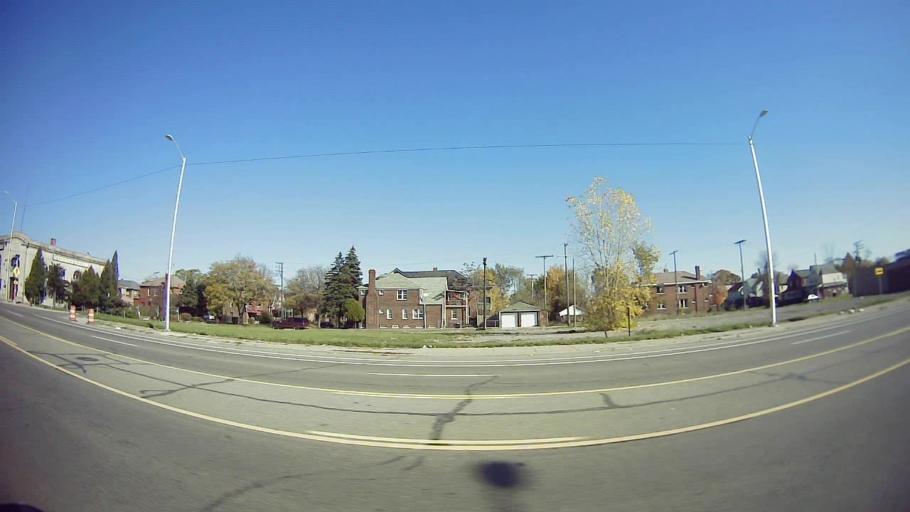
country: US
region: Michigan
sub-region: Wayne County
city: Highland Park
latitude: 42.3792
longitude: -83.1239
